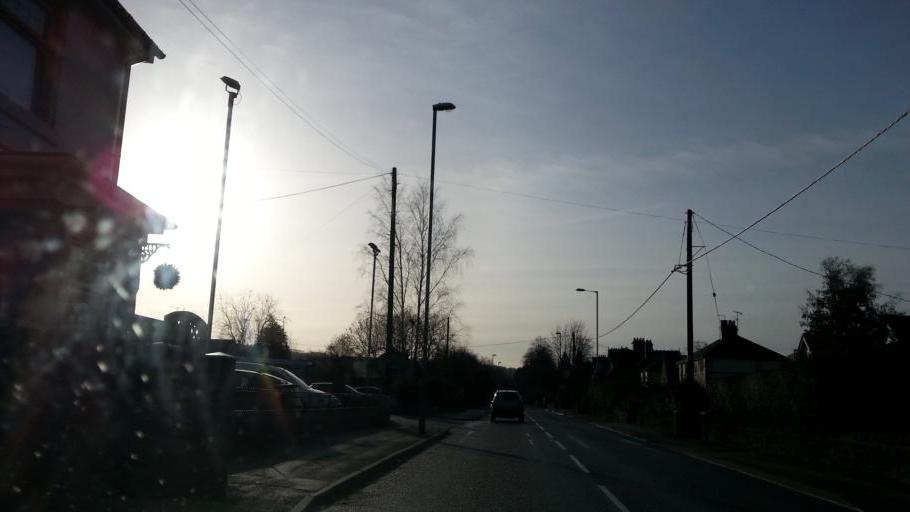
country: GB
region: England
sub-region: Staffordshire
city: Biddulph
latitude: 53.0709
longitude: -2.1171
